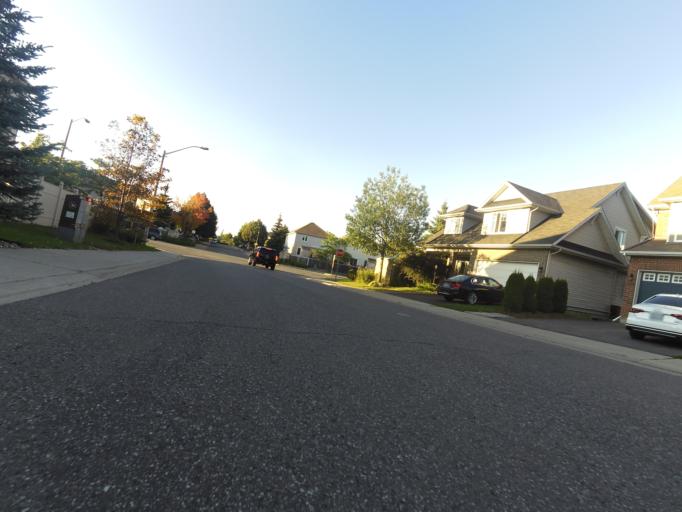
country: CA
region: Ontario
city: Ottawa
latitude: 45.2860
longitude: -75.7055
